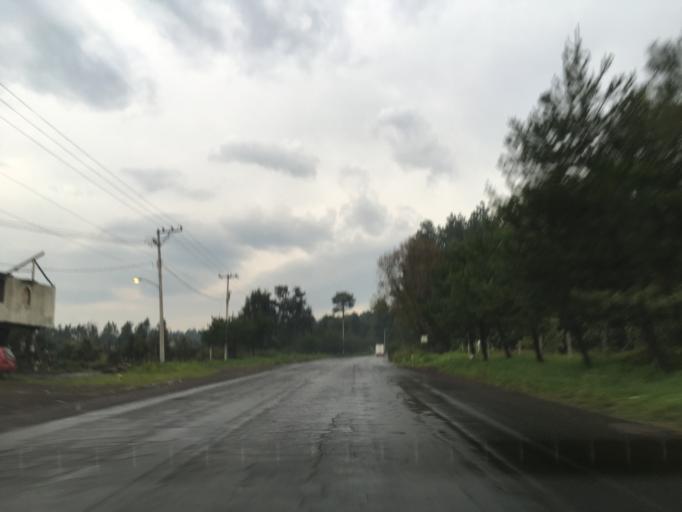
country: MX
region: Michoacan
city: Capacuaro
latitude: 19.5317
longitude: -102.0829
